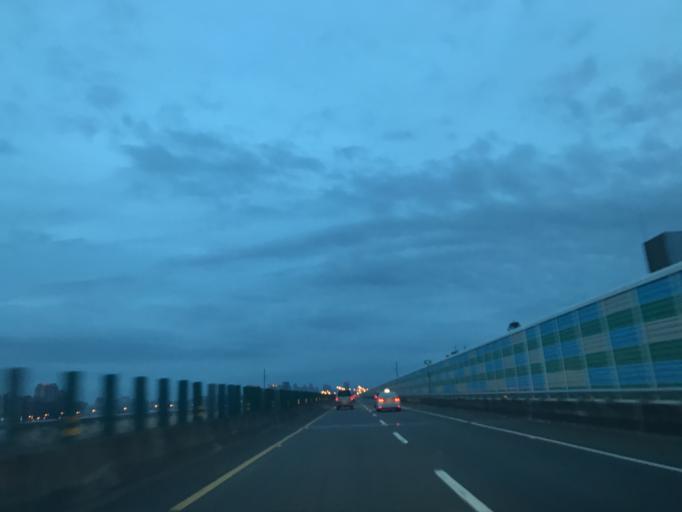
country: TW
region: Taiwan
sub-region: Hsinchu
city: Hsinchu
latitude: 24.8229
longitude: 120.9846
